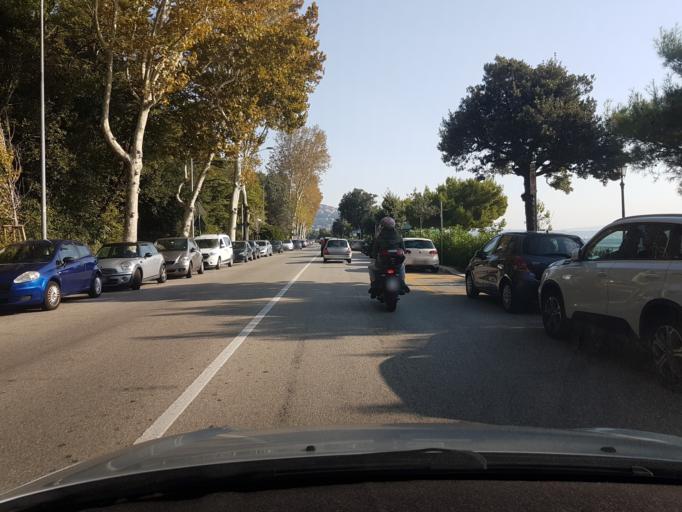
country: IT
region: Friuli Venezia Giulia
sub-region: Provincia di Trieste
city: Prosecco-Contovello
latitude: 45.6908
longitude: 13.7411
